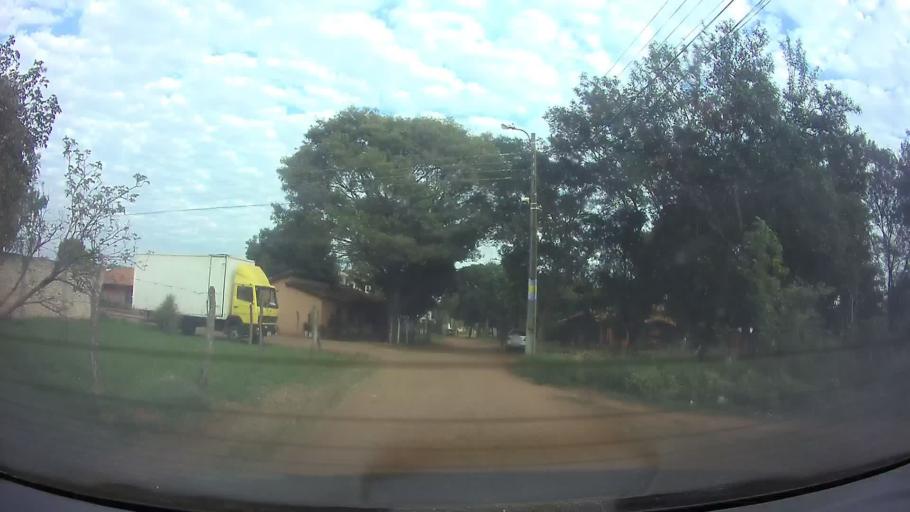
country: PY
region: Central
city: Limpio
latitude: -25.2514
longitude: -57.5062
